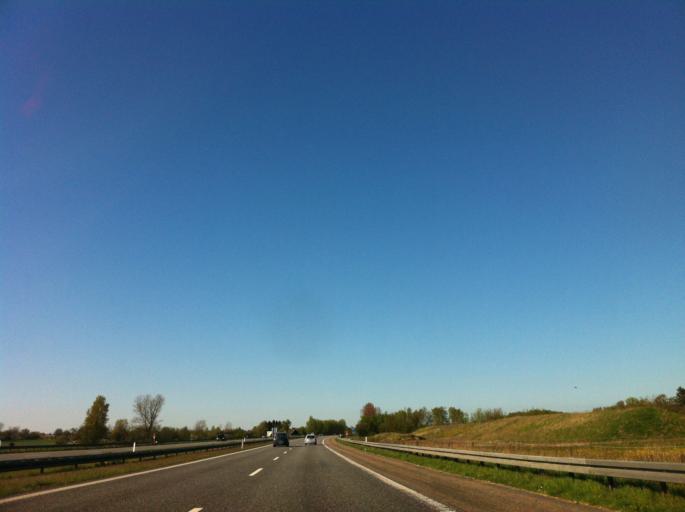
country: DK
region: Zealand
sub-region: Faxe Kommune
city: Ronnede
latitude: 55.2721
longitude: 12.0079
